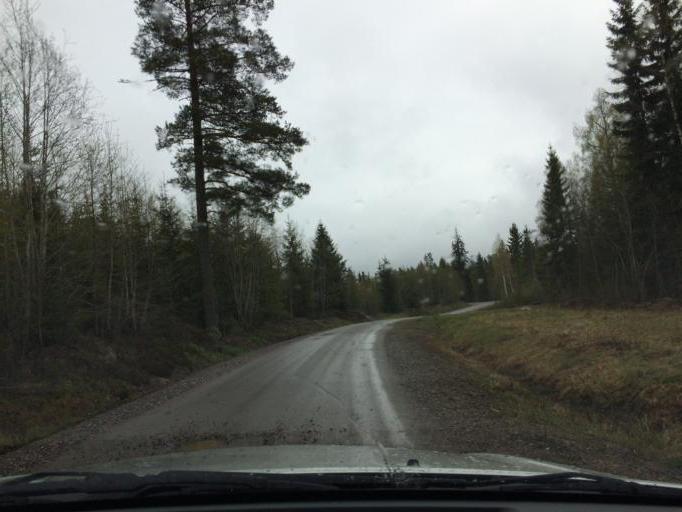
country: SE
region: OErebro
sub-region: Hallefors Kommun
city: Haellefors
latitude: 60.0199
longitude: 14.5835
